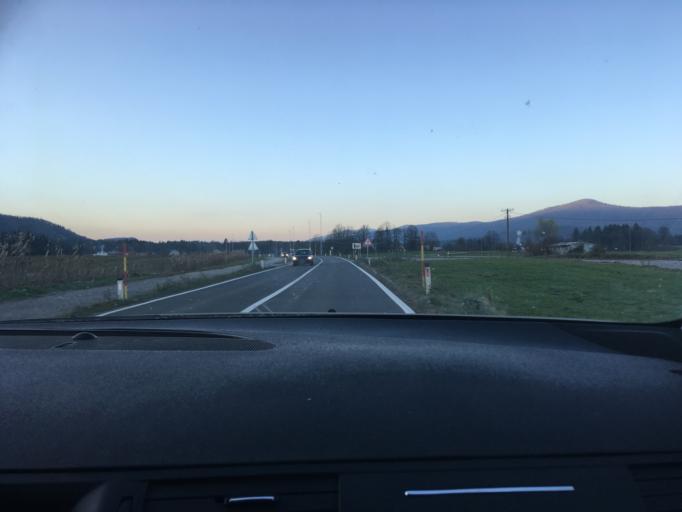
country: SI
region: Kocevje
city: Kocevje
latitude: 45.6702
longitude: 14.8363
